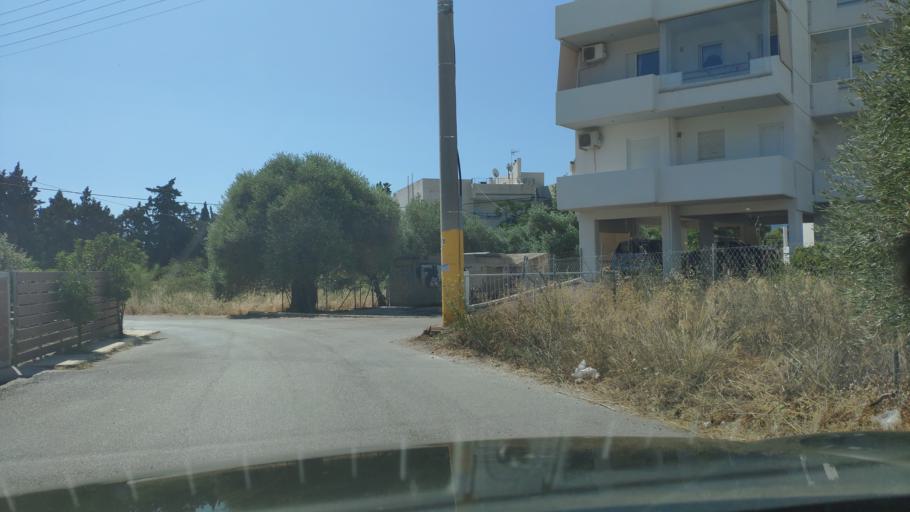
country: GR
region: Attica
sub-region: Nomarchia Anatolikis Attikis
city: Limin Mesoyaias
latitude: 37.8936
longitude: 24.0252
